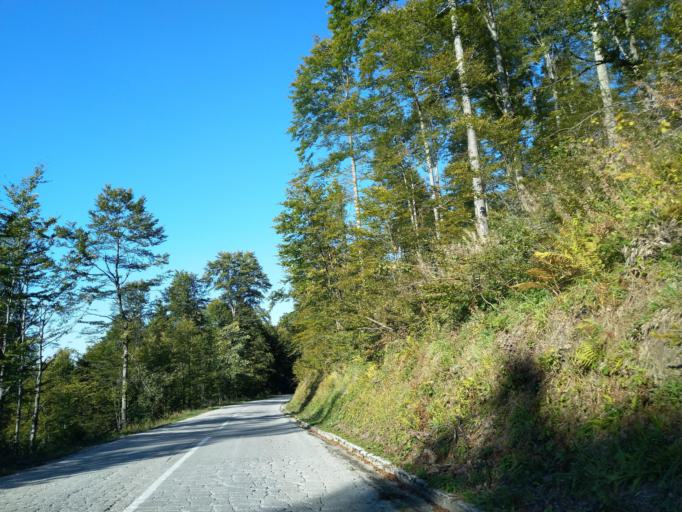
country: RS
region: Central Serbia
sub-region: Moravicki Okrug
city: Ivanjica
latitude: 43.4358
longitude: 20.2678
